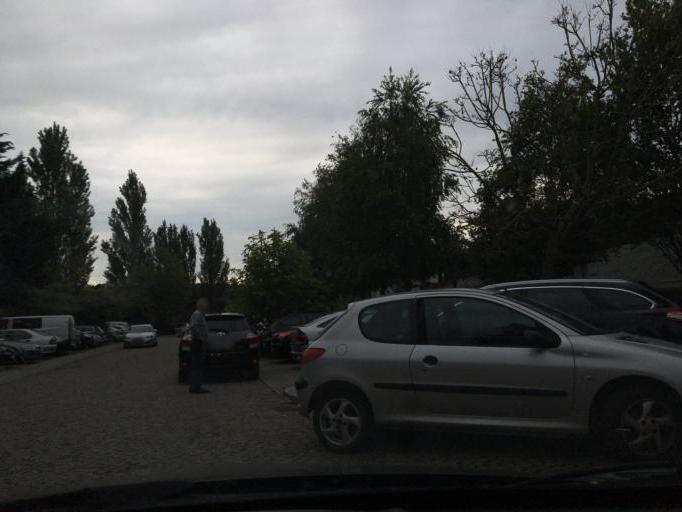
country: PT
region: Porto
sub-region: Maia
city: Anta
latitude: 41.2831
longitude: -8.6097
